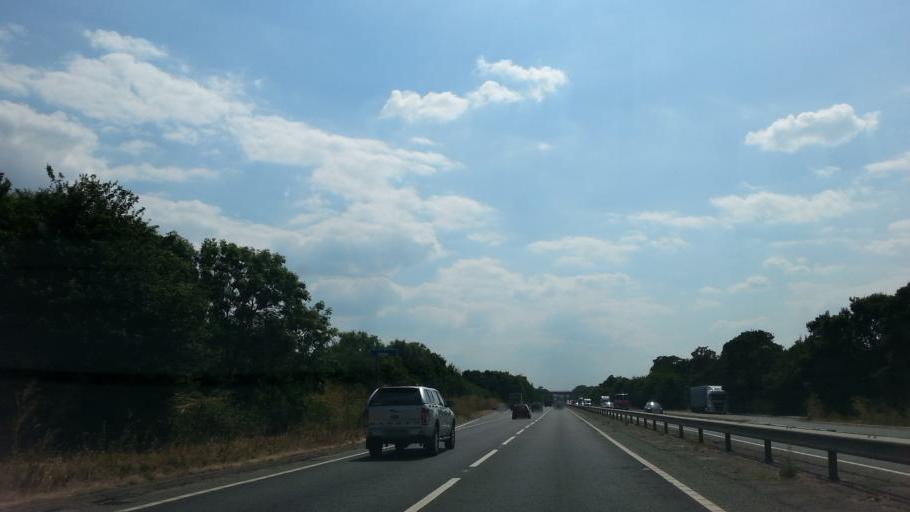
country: GB
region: England
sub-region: Cambridgeshire
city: Isleham
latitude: 52.2928
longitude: 0.4738
